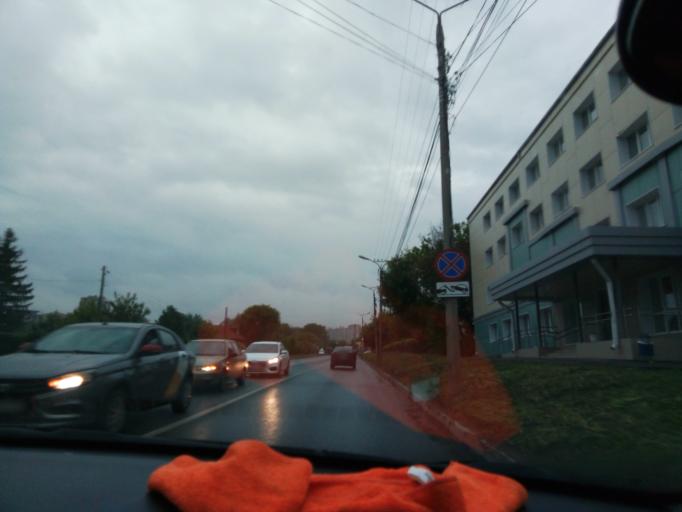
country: RU
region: Chuvashia
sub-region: Cheboksarskiy Rayon
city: Cheboksary
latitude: 56.1412
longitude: 47.2524
